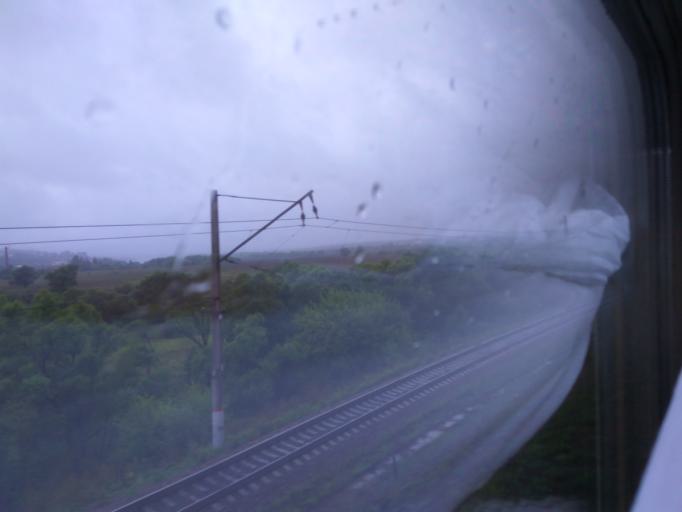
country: RU
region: Moskovskaya
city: Kashira
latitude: 54.8563
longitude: 38.1756
